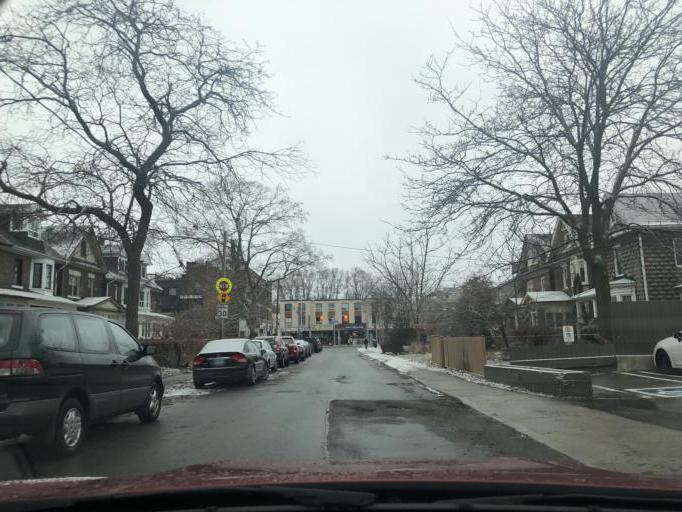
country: CA
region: Ontario
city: Toronto
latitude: 43.6805
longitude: -79.3422
